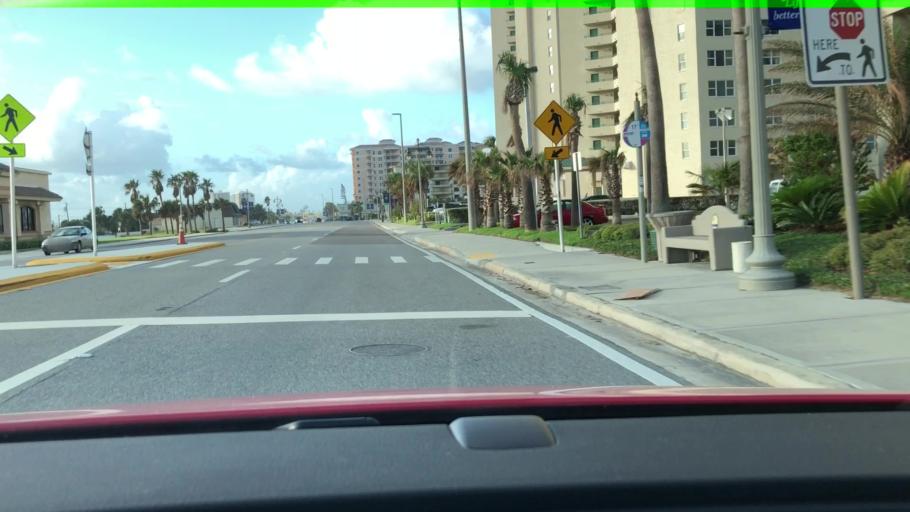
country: US
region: Florida
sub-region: Volusia County
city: Daytona Beach Shores
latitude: 29.1543
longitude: -80.9707
